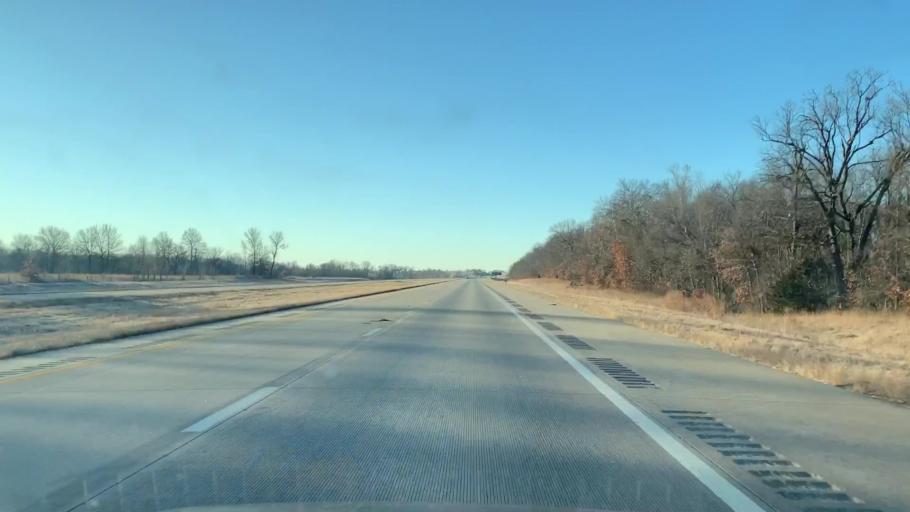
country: US
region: Kansas
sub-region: Linn County
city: Pleasanton
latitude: 38.0177
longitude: -94.7039
